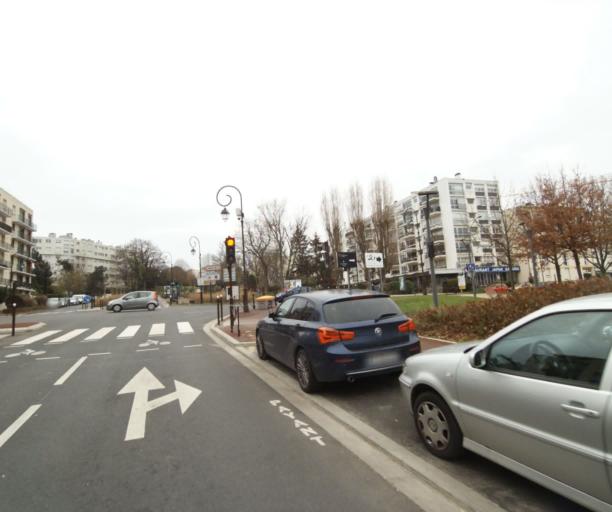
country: FR
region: Ile-de-France
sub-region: Departement des Hauts-de-Seine
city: Saint-Cloud
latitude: 48.8521
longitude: 2.2056
